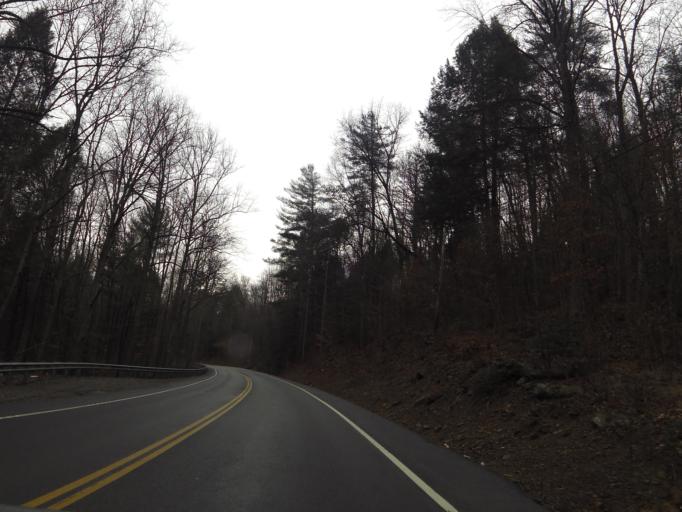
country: US
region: Tennessee
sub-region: Morgan County
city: Wartburg
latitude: 36.0371
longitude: -84.5254
